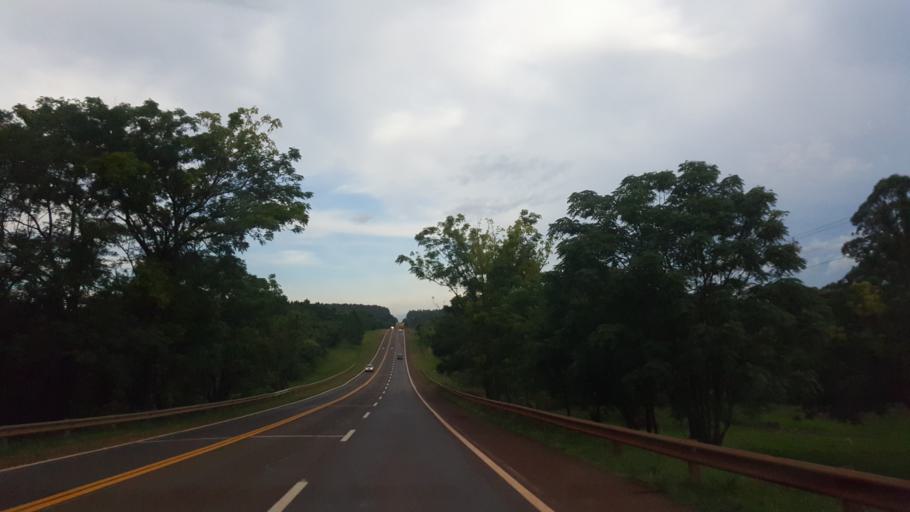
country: AR
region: Misiones
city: Jardin America
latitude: -27.0827
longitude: -55.2855
